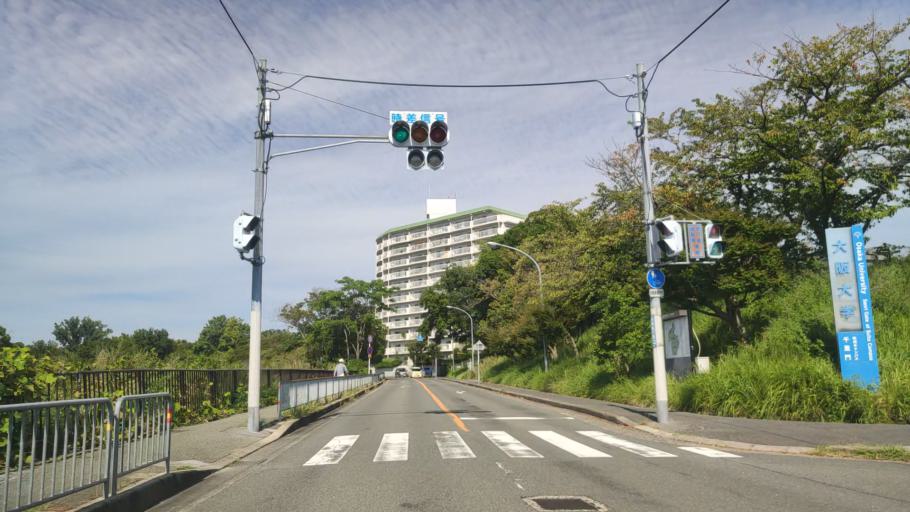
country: JP
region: Osaka
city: Mino
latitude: 34.8228
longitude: 135.5192
